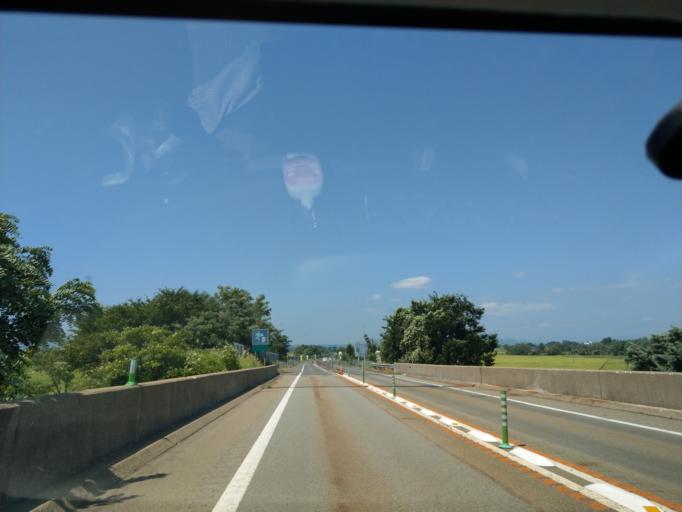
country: JP
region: Akita
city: Yokotemachi
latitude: 39.3335
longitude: 140.5055
